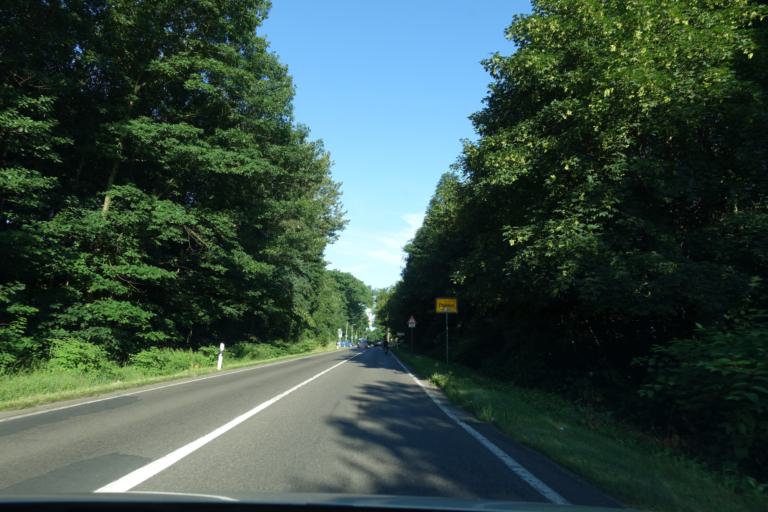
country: DE
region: Saxony
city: Hilbersdorf
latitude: 50.8548
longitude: 12.9694
